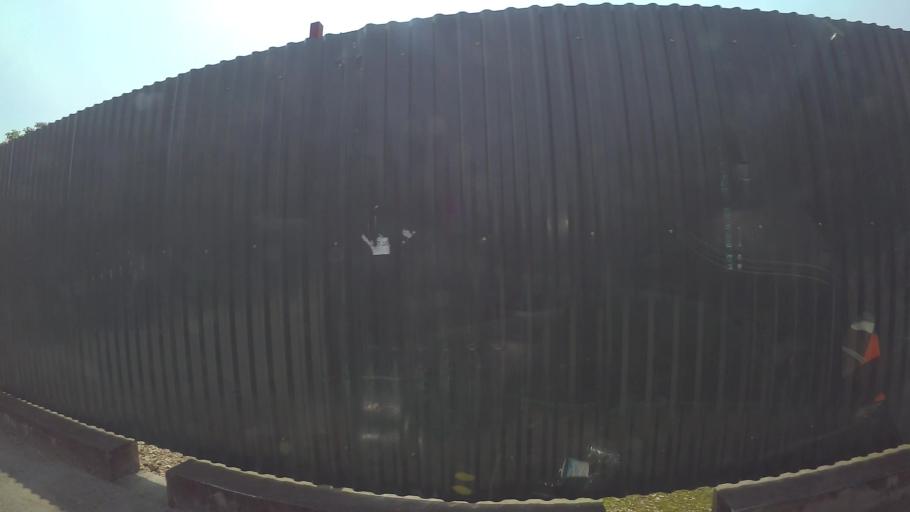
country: VN
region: Ha Noi
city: Trau Quy
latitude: 21.0287
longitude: 105.9083
